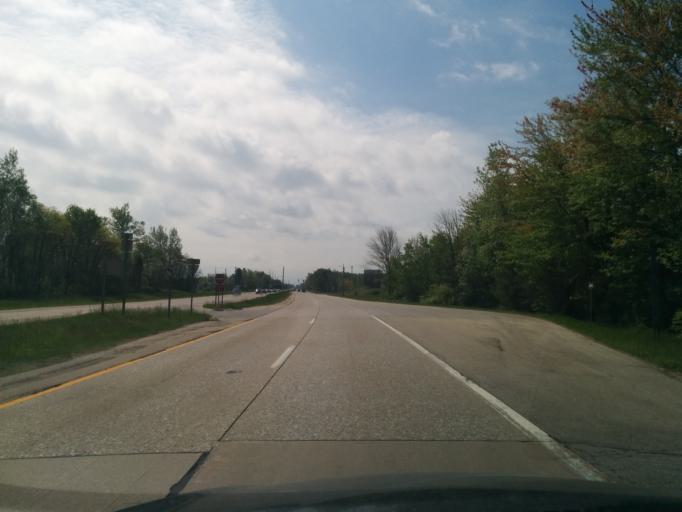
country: US
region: Michigan
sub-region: Ottawa County
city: Grand Haven
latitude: 43.0324
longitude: -86.2197
